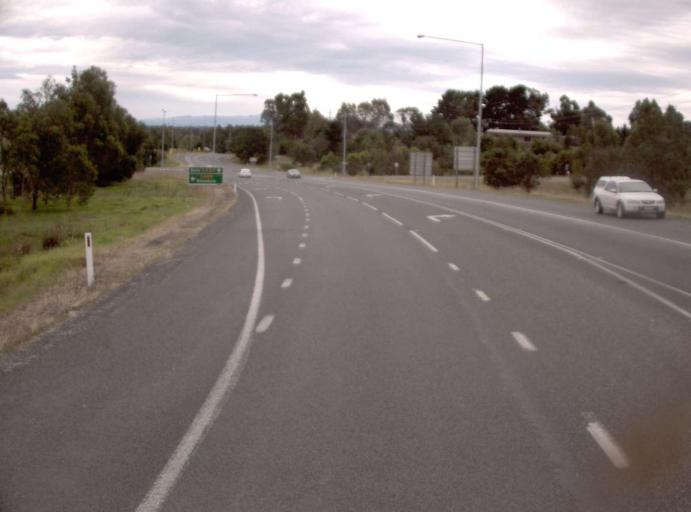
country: AU
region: Victoria
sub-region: Wellington
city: Sale
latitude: -38.1610
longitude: 147.0858
